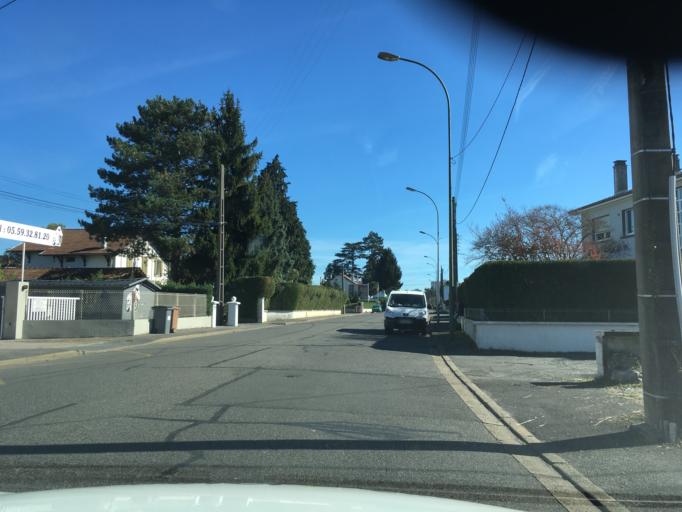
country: FR
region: Aquitaine
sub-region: Departement des Pyrenees-Atlantiques
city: Lons
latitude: 43.3243
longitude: -0.3769
